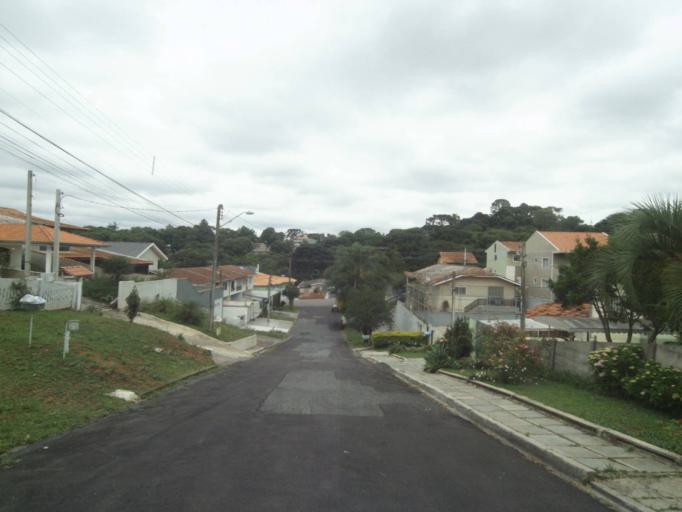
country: BR
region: Parana
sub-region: Curitiba
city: Curitiba
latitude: -25.3979
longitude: -49.2851
